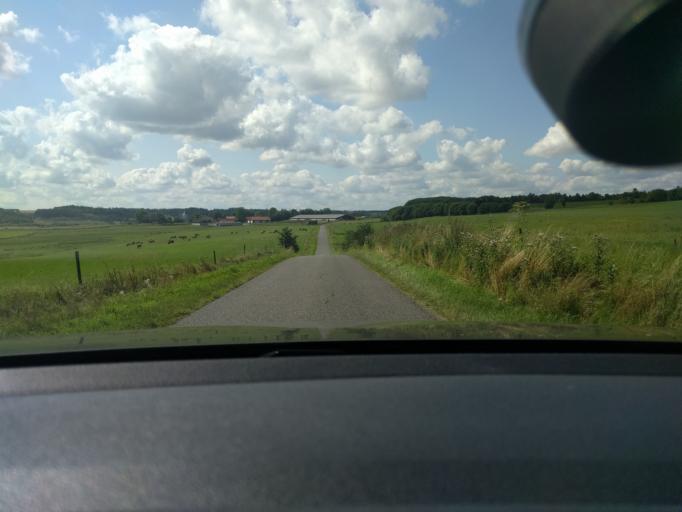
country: DK
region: Central Jutland
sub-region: Viborg Kommune
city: Bjerringbro
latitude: 56.4584
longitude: 9.5901
